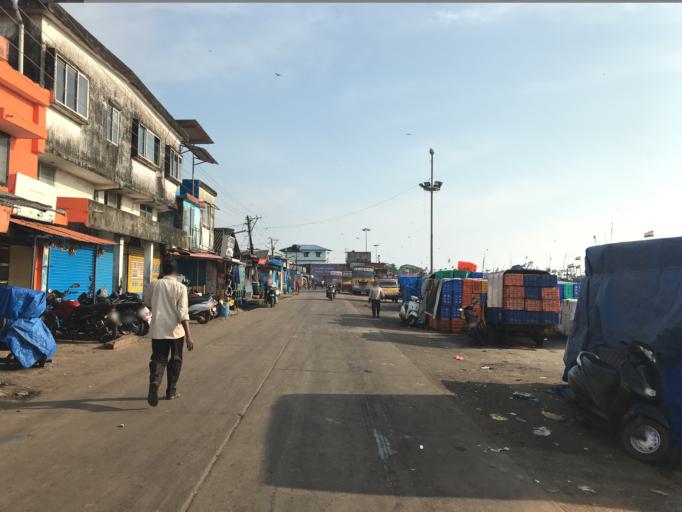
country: IN
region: Karnataka
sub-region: Dakshina Kannada
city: Ullal
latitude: 12.8567
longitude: 74.8329
